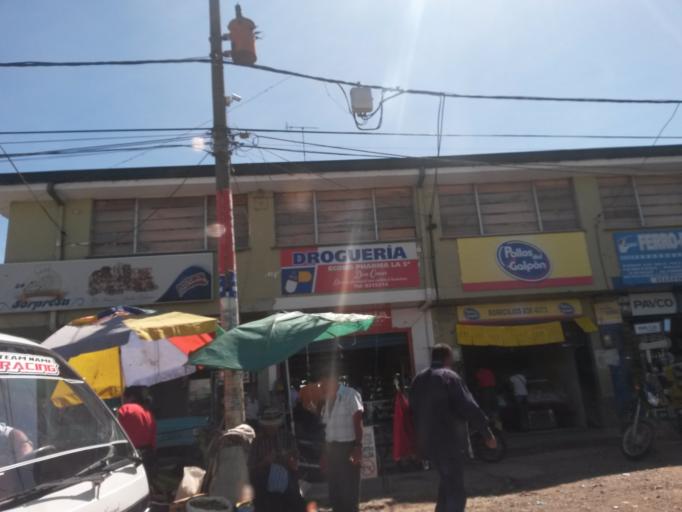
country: CO
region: Cauca
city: Popayan
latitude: 2.4452
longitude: -76.6156
